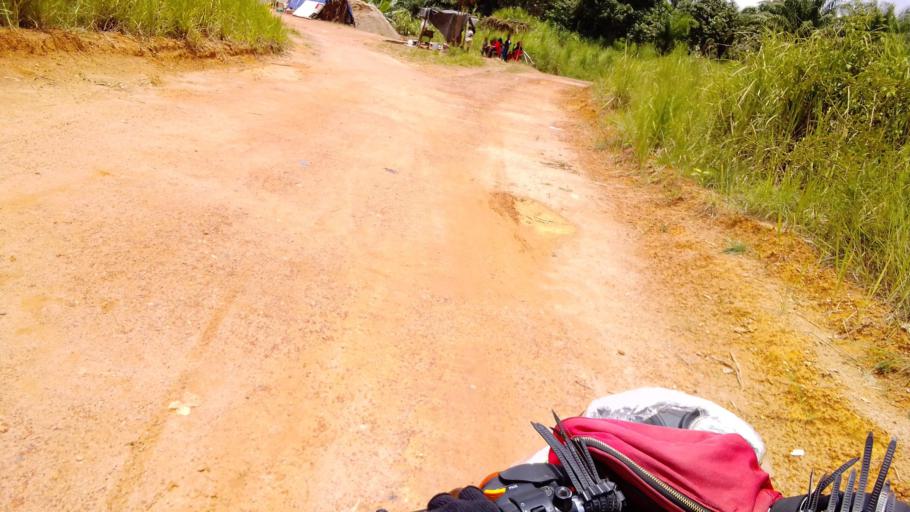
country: SL
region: Eastern Province
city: Koidu
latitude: 8.6803
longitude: -10.9551
